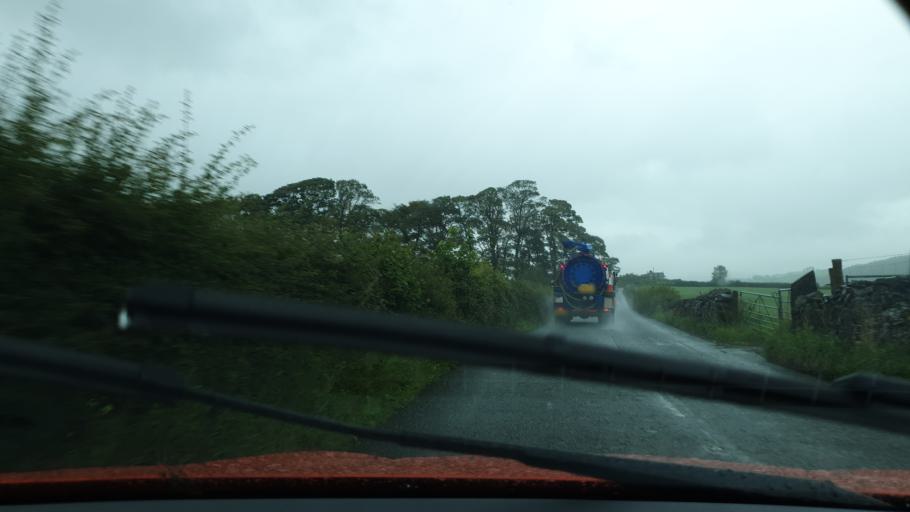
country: GB
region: England
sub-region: Cumbria
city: Millom
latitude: 54.2749
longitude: -3.2218
